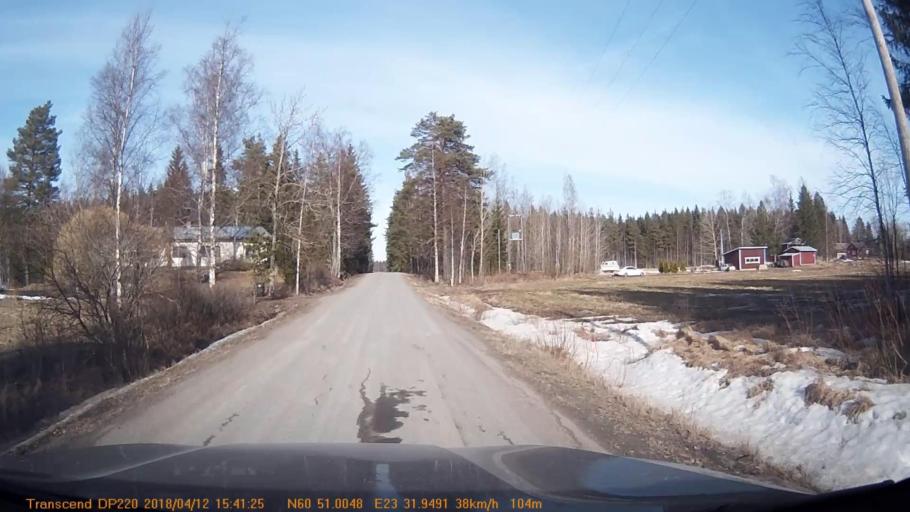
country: FI
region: Haeme
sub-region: Forssa
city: Jokioinen
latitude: 60.8503
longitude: 23.5330
